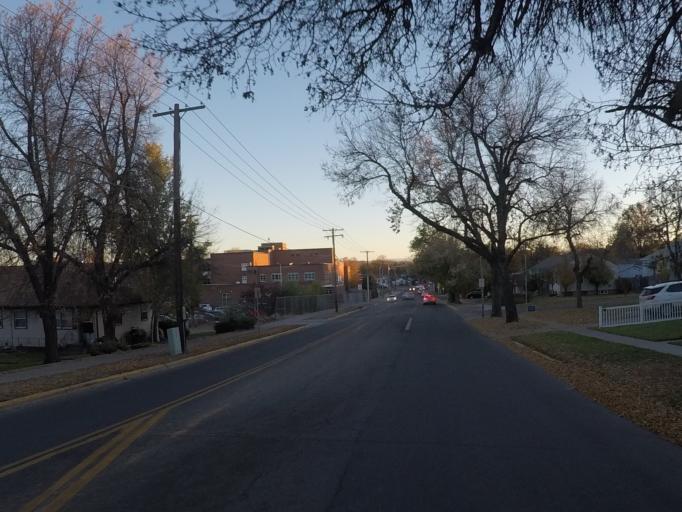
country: US
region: Montana
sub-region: Yellowstone County
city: Billings
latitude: 45.7864
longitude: -108.5279
